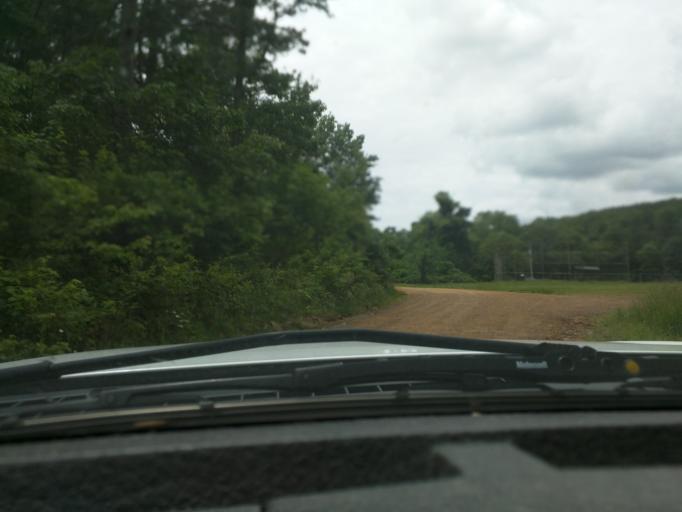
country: US
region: Arkansas
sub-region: Madison County
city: Huntsville
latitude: 35.8659
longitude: -93.5308
